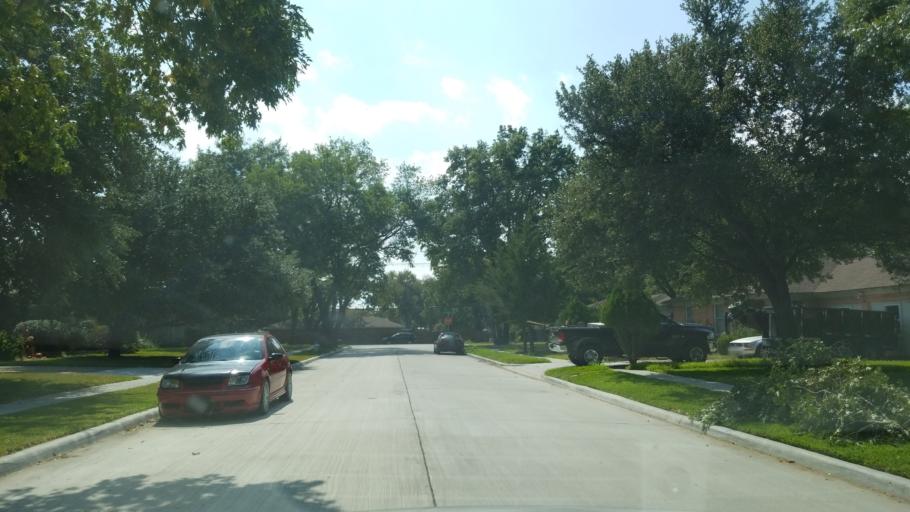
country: US
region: Texas
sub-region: Dallas County
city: Garland
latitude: 32.8952
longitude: -96.6578
